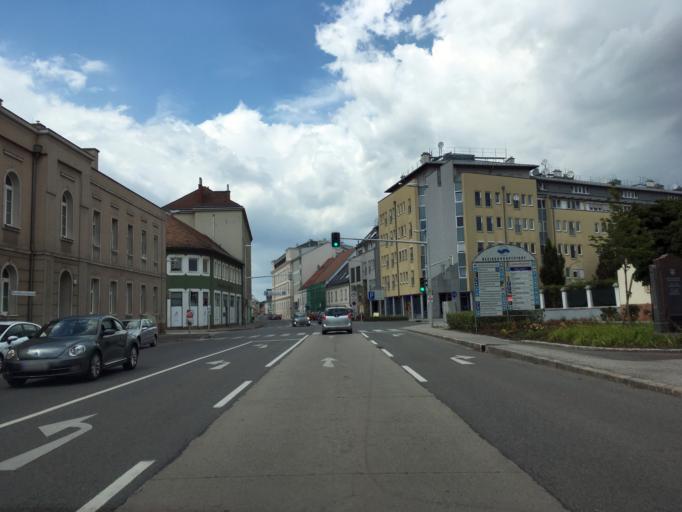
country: AT
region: Lower Austria
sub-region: Politischer Bezirk Korneuburg
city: Korneuburg
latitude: 48.3418
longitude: 16.3355
